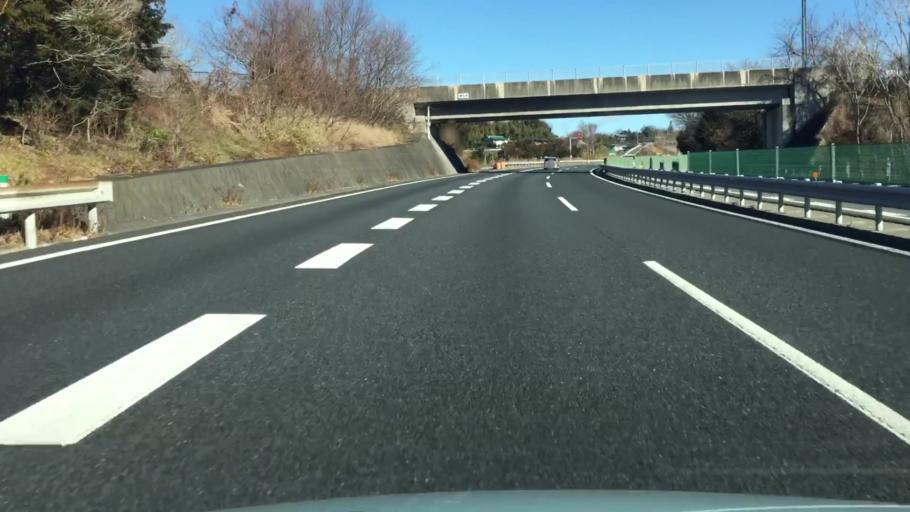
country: JP
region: Gunma
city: Shibukawa
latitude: 36.5132
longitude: 139.0325
